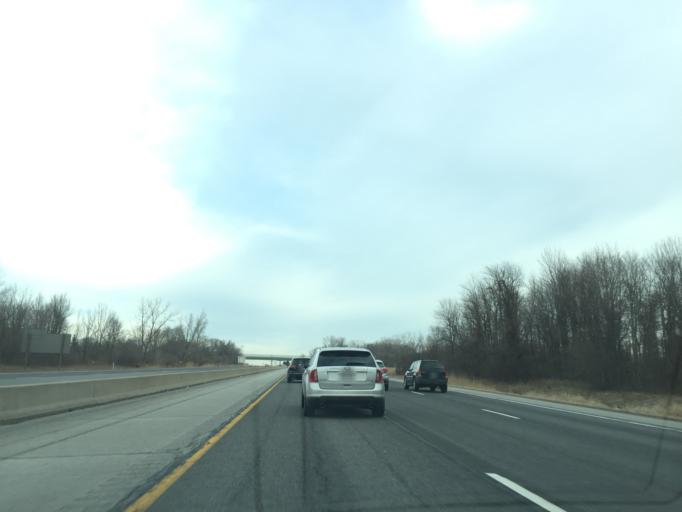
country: US
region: Indiana
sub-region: LaPorte County
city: Trail Creek
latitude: 41.7022
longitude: -86.8074
